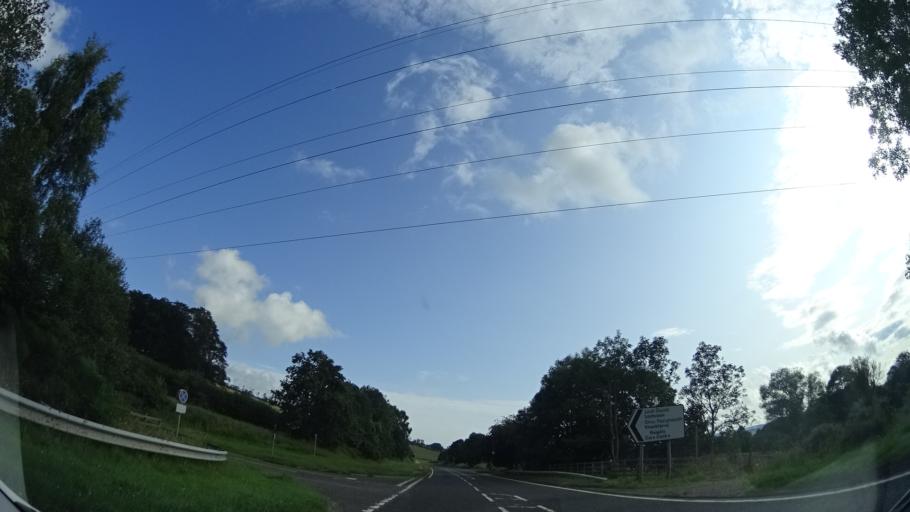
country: GB
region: Scotland
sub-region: Highland
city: Conon Bridge
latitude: 57.5749
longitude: -4.4505
